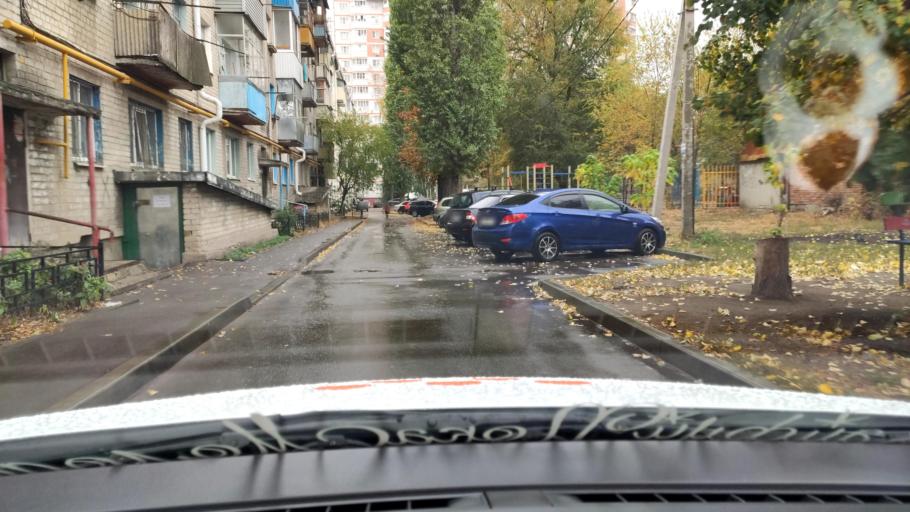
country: RU
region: Voronezj
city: Voronezh
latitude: 51.6724
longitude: 39.1520
